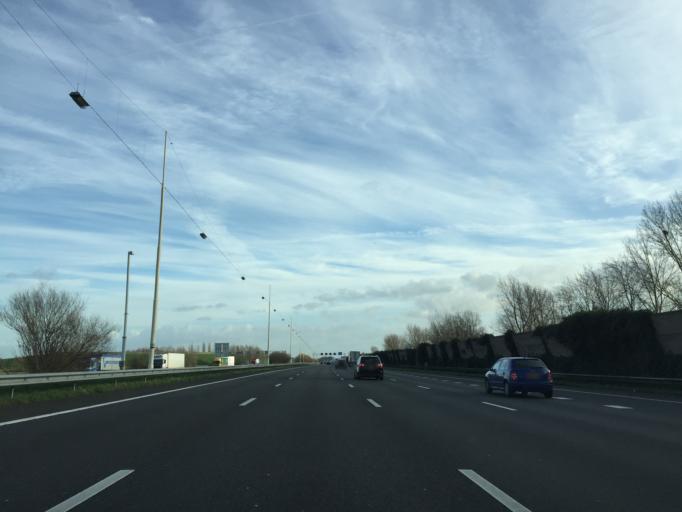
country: NL
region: Utrecht
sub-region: Gemeente Montfoort
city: Montfoort
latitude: 52.0794
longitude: 4.9957
